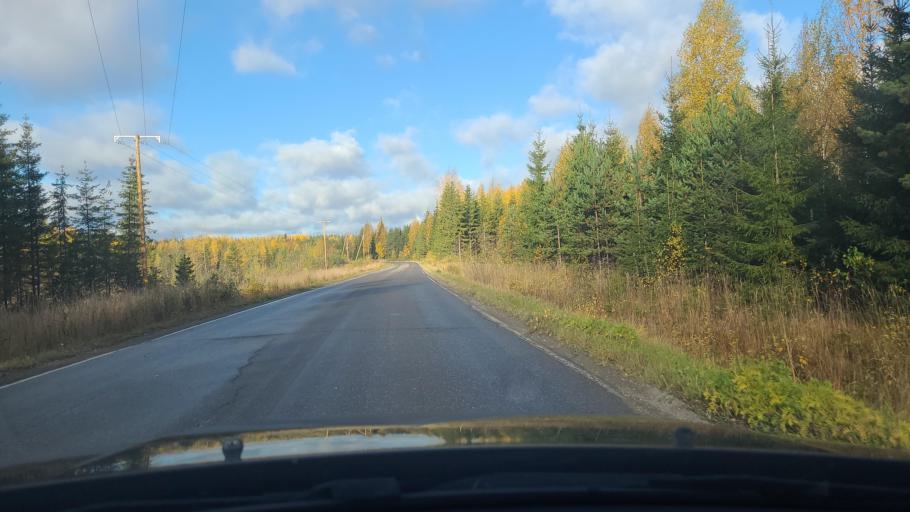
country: FI
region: Southern Savonia
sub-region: Pieksaemaeki
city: Juva
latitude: 61.8810
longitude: 27.7581
